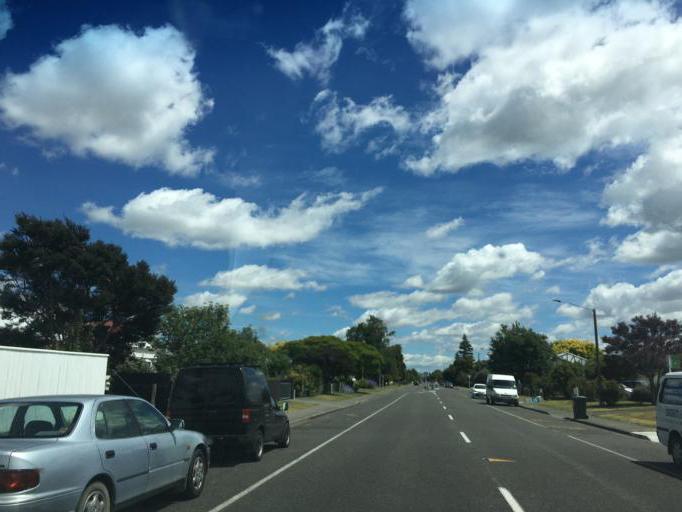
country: NZ
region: Hawke's Bay
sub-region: Hastings District
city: Hastings
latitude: -39.6463
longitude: 176.8586
